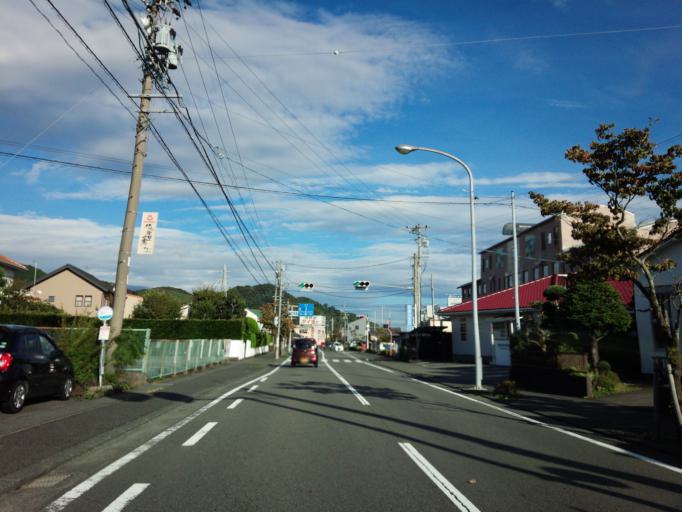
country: JP
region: Shizuoka
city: Shimada
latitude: 34.8410
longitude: 138.1784
